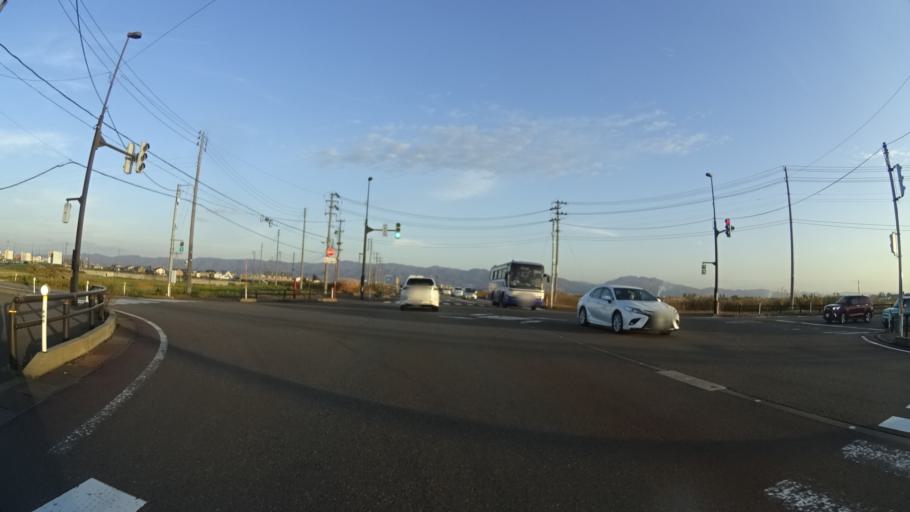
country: JP
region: Niigata
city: Nagaoka
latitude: 37.4361
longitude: 138.8041
